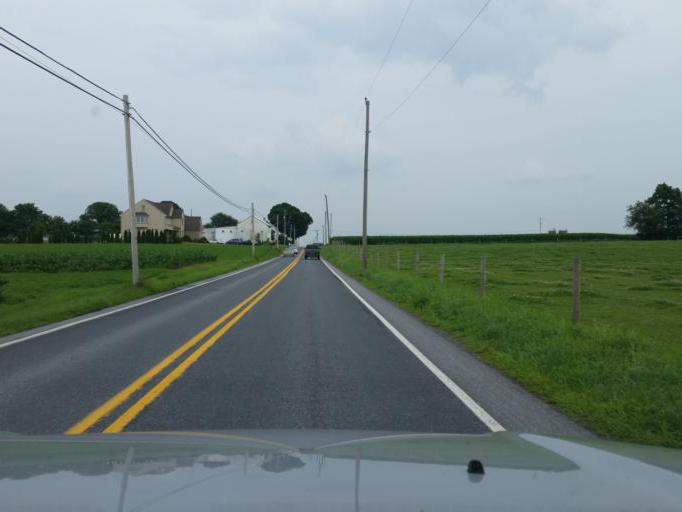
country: US
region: Pennsylvania
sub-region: Lancaster County
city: Lititz
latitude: 40.1570
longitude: -76.3462
